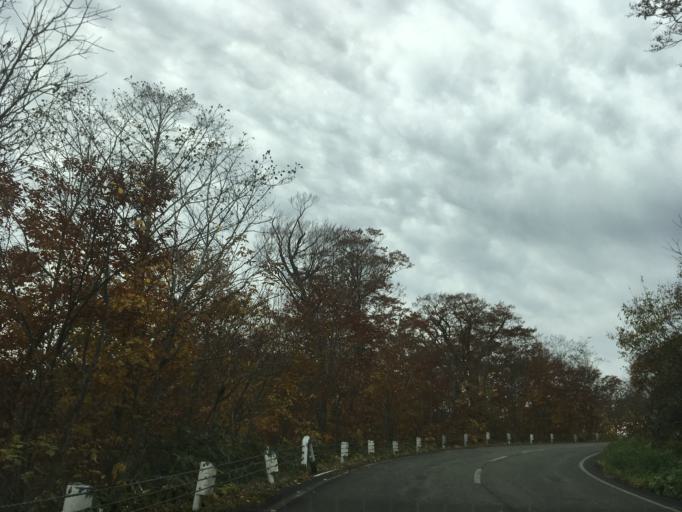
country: JP
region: Akita
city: Yuzawa
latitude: 38.9412
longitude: 140.7179
